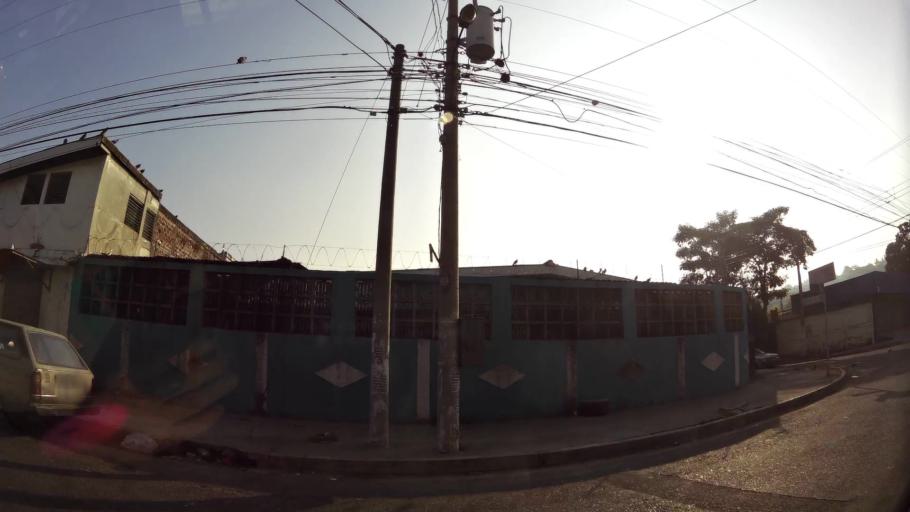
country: SV
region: La Libertad
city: Antiguo Cuscatlan
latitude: 13.6827
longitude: -89.2248
